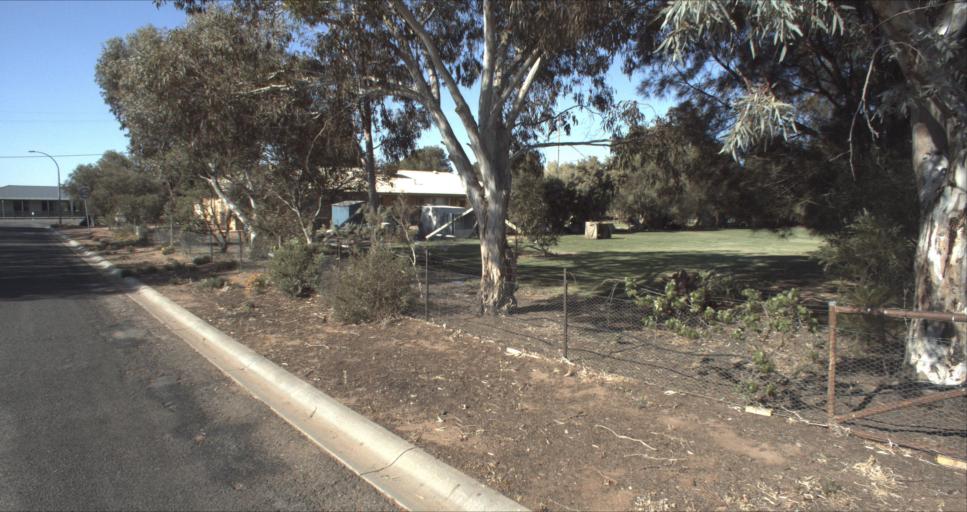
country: AU
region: New South Wales
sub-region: Leeton
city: Leeton
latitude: -34.5357
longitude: 146.4157
